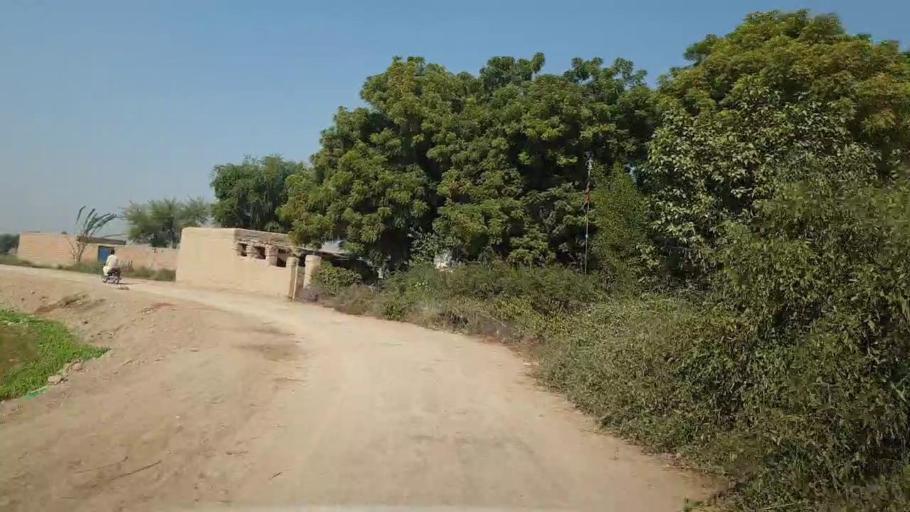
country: PK
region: Sindh
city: Bhan
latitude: 26.6409
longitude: 67.7174
